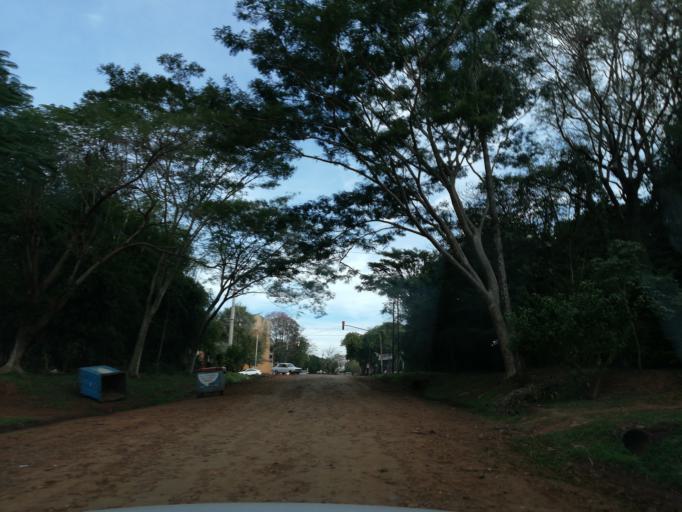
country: AR
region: Misiones
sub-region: Departamento de Capital
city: Posadas
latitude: -27.3564
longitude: -55.9303
